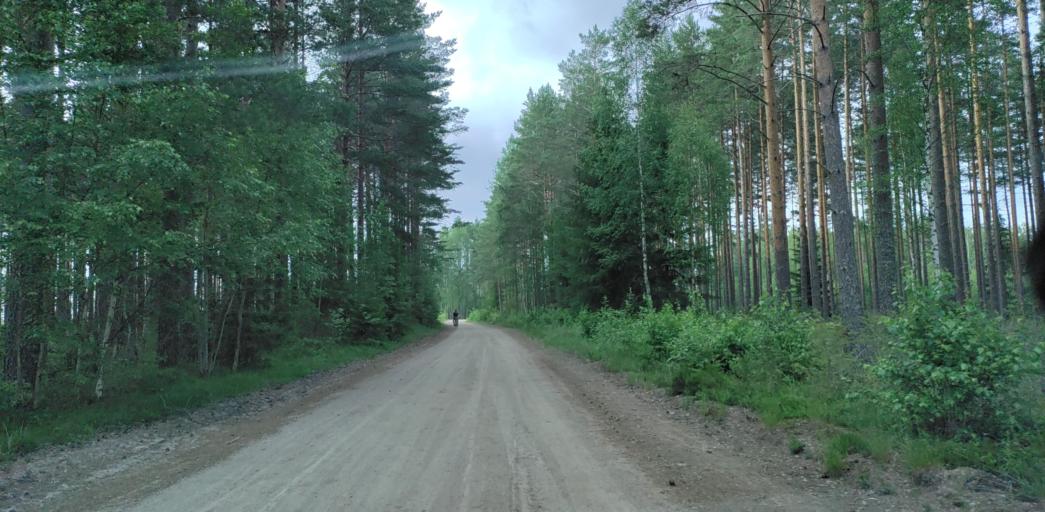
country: SE
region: Vaermland
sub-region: Hagfors Kommun
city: Hagfors
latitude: 60.0550
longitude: 13.5787
